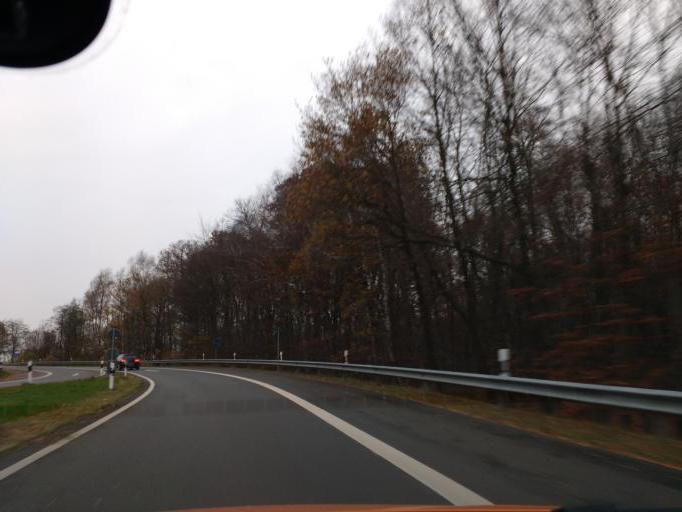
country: DE
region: Lower Saxony
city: Hude
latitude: 53.0610
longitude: 8.4682
